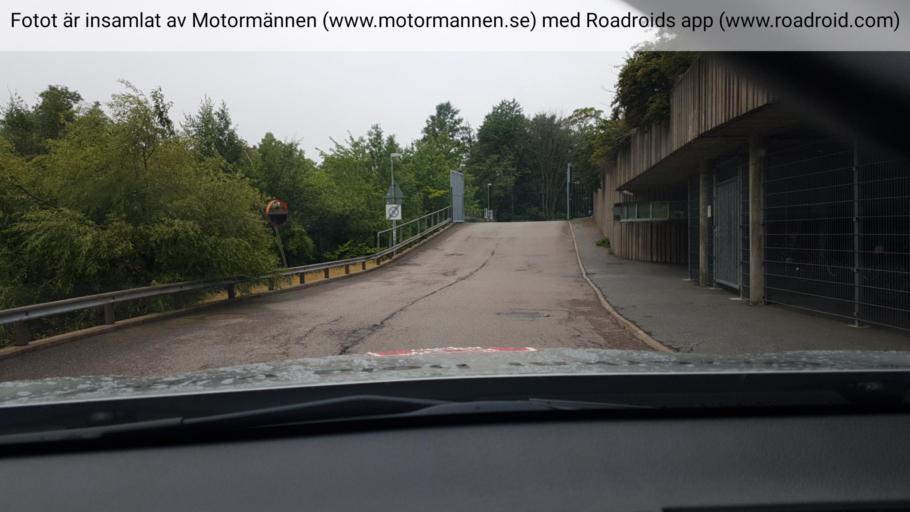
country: SE
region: Vaestra Goetaland
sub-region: Goteborg
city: Goeteborg
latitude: 57.7277
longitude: 12.0141
